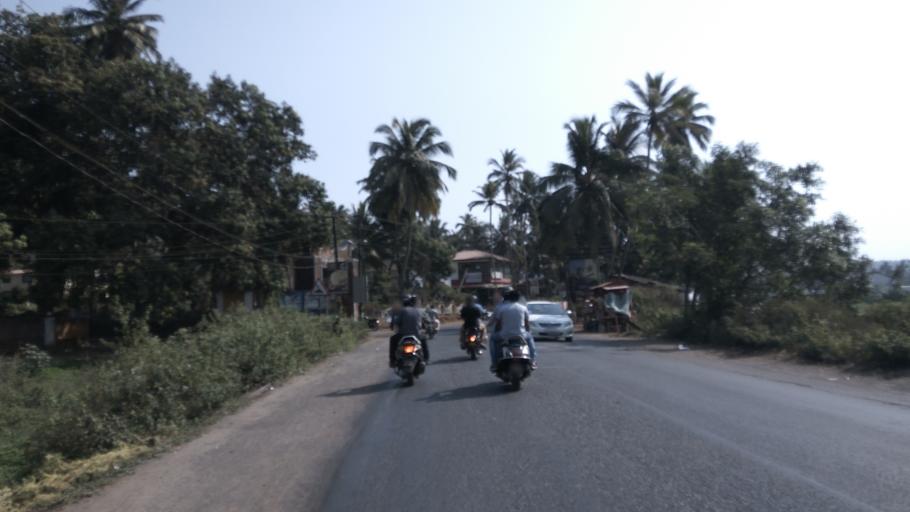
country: IN
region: Goa
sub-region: North Goa
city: Saligao
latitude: 15.5456
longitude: 73.7833
